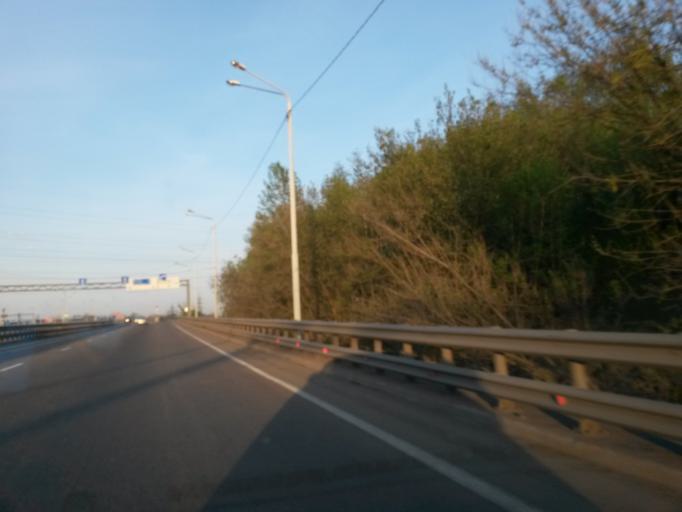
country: RU
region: Jaroslavl
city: Yaroslavl
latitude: 57.6684
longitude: 39.8340
